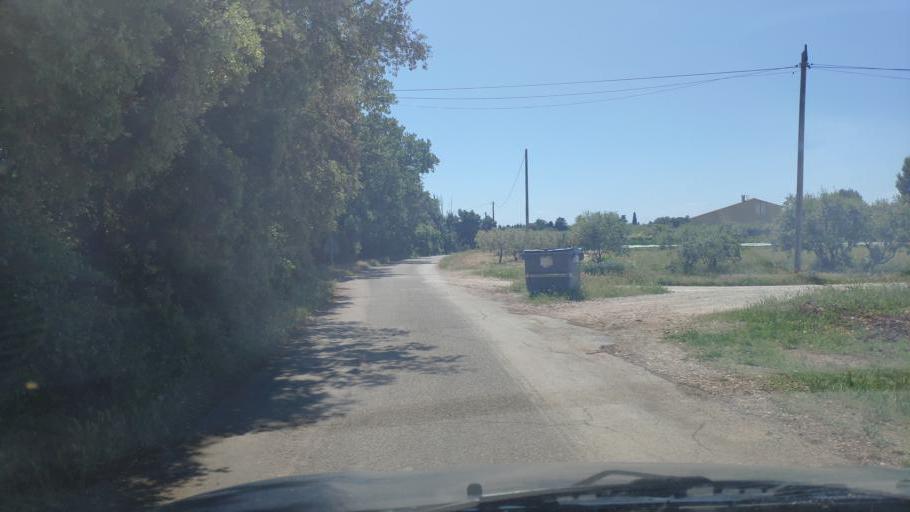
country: FR
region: Provence-Alpes-Cote d'Azur
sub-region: Departement du Vaucluse
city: Carpentras
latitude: 44.0704
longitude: 5.0355
